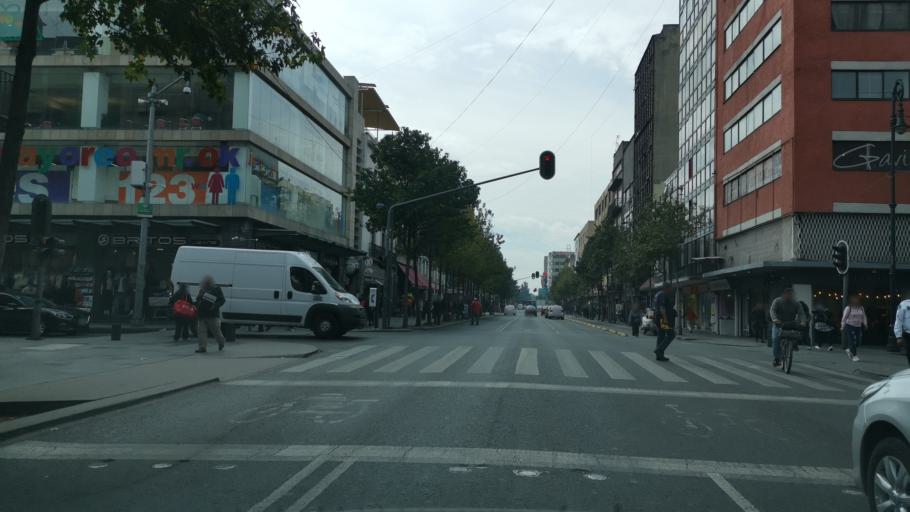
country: MX
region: Mexico City
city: Mexico City
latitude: 19.4285
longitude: -99.1327
